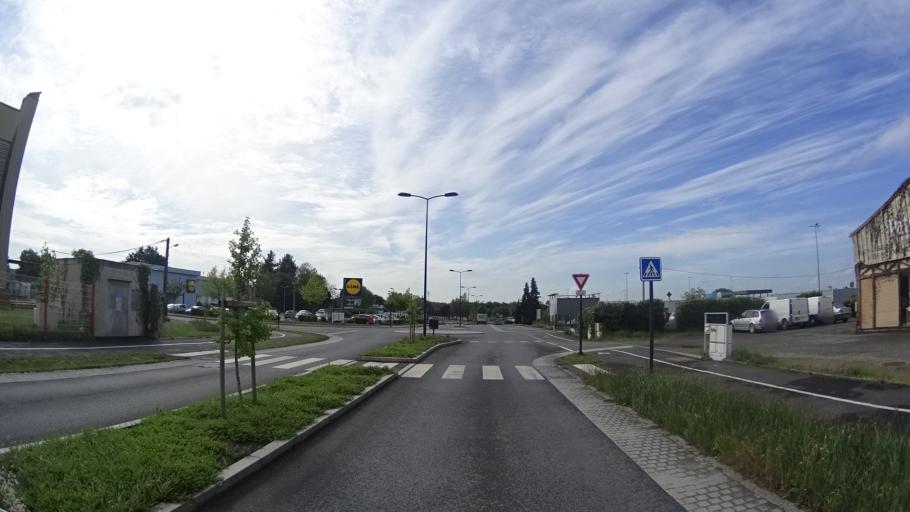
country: FR
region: Brittany
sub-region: Departement d'Ille-et-Vilaine
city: Mordelles
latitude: 48.0809
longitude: -1.8358
